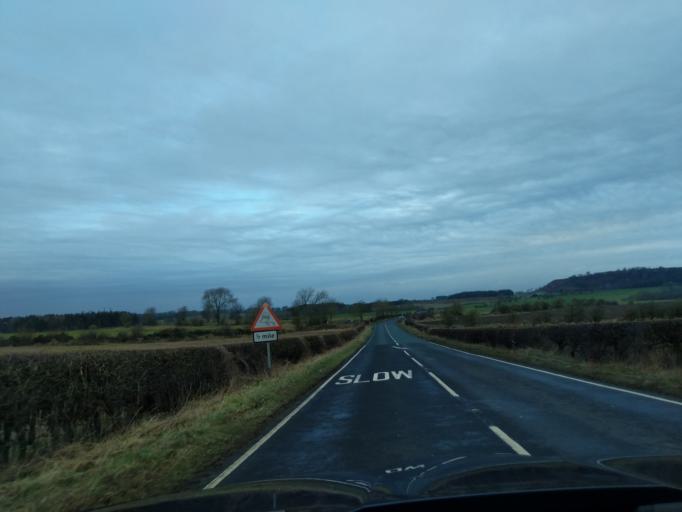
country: GB
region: England
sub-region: Northumberland
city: Rothley
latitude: 55.1182
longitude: -1.9066
